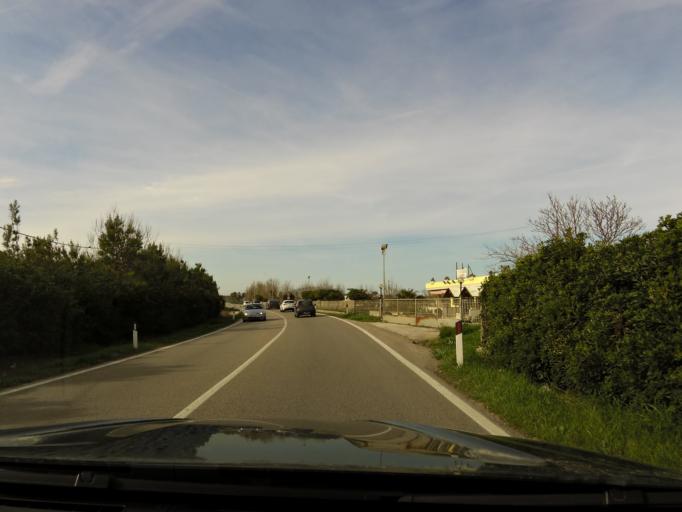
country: IT
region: The Marches
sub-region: Provincia di Macerata
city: Porto Potenza Picena
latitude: 43.3877
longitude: 13.6851
